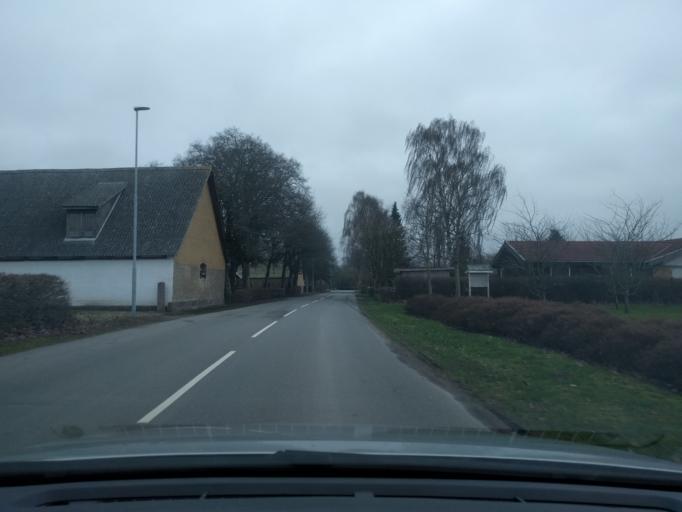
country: DK
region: South Denmark
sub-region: Odense Kommune
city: Neder Holluf
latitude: 55.3743
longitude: 10.5047
